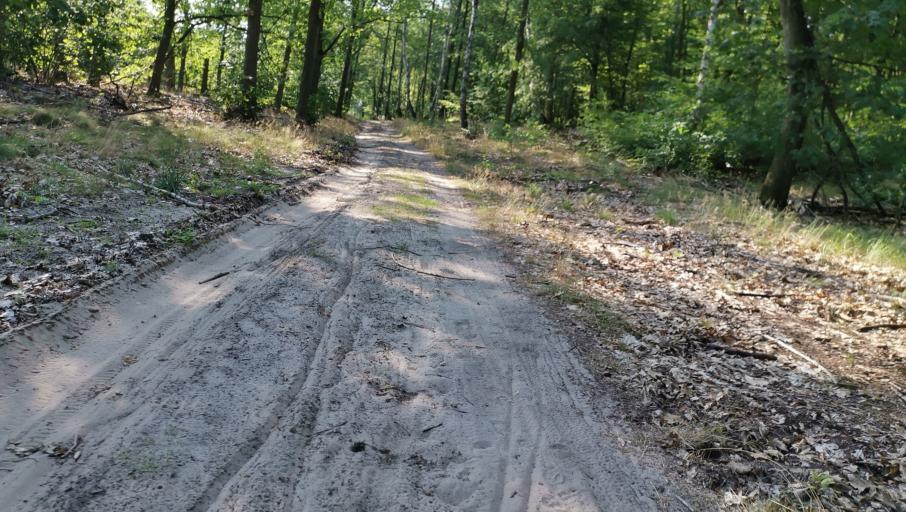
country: DE
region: Brandenburg
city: Werder
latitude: 52.3854
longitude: 12.9853
